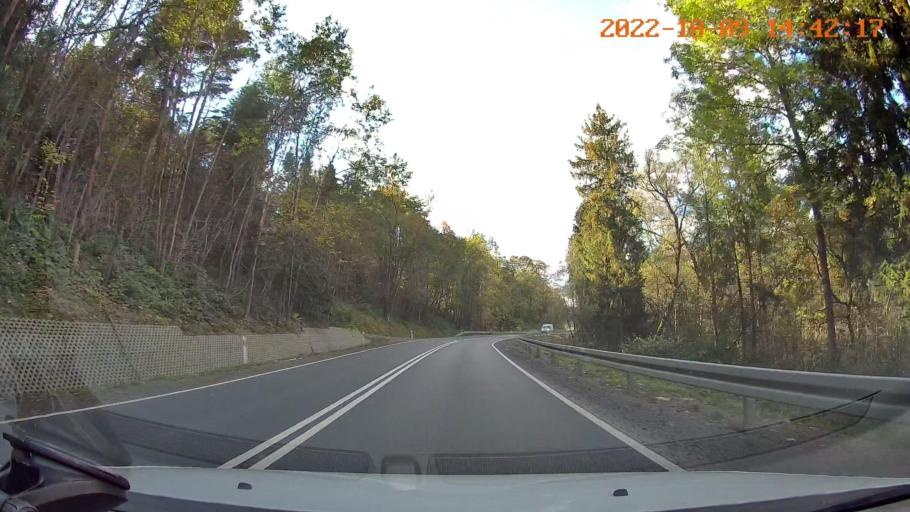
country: PL
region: Lesser Poland Voivodeship
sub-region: Powiat myslenicki
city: Lubien
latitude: 49.7131
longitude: 20.0000
